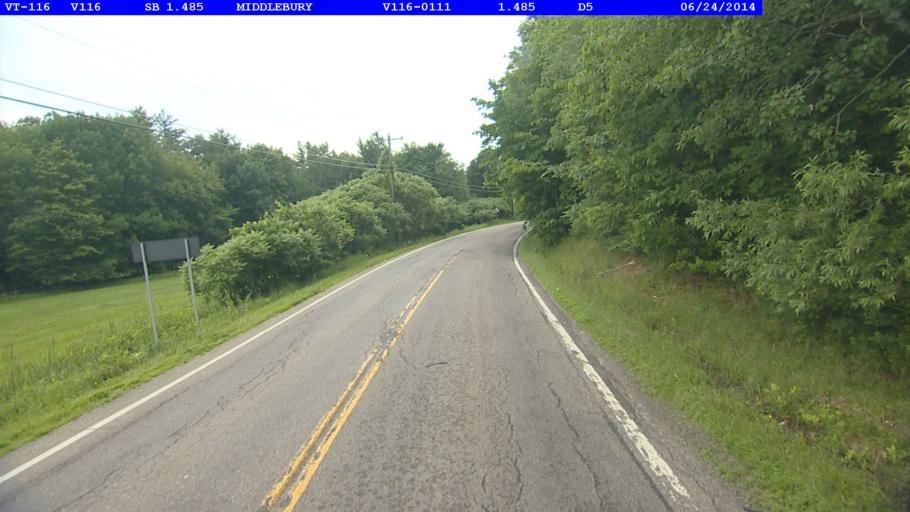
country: US
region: Vermont
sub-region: Addison County
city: Middlebury (village)
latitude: 43.9860
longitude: -73.1040
